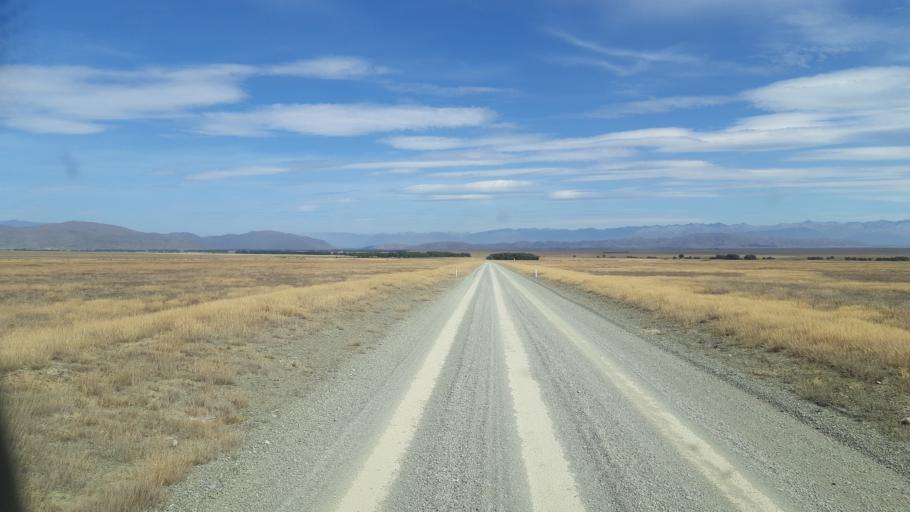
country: NZ
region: Canterbury
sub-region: Timaru District
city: Pleasant Point
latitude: -44.1949
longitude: 170.5299
